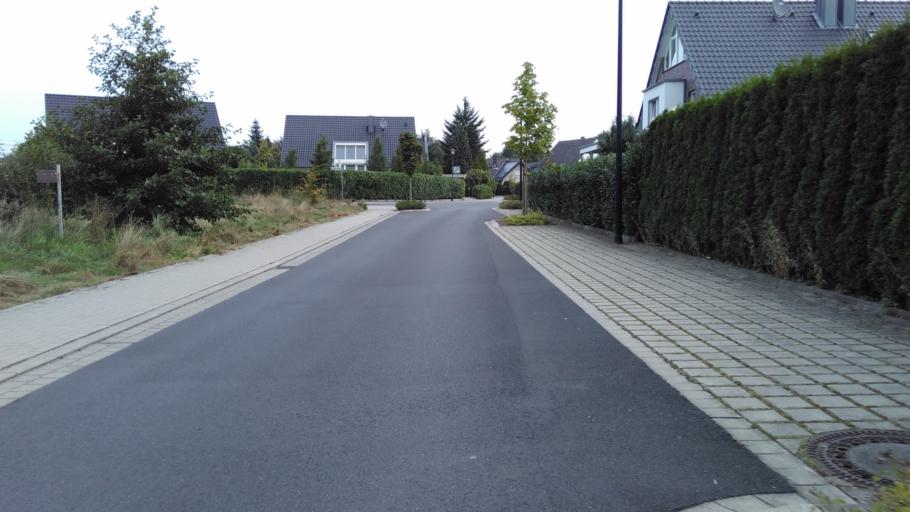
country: DE
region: North Rhine-Westphalia
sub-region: Regierungsbezirk Detmold
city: Verl
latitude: 51.8741
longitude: 8.4941
